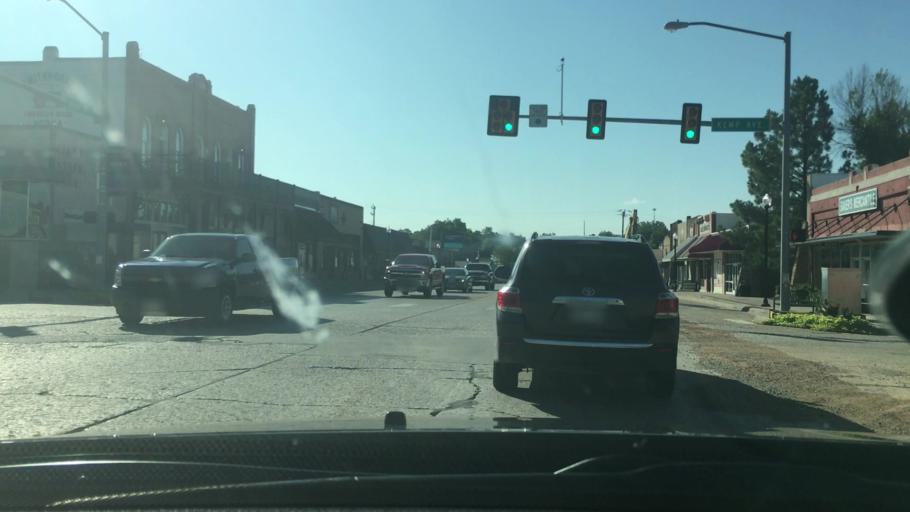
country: US
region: Oklahoma
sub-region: Johnston County
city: Tishomingo
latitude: 34.2360
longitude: -96.6796
